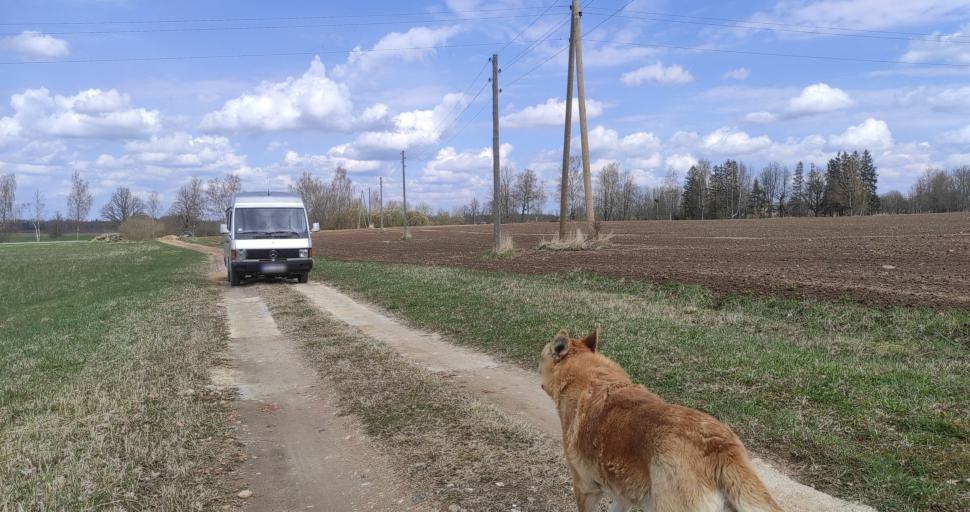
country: LV
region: Talsu Rajons
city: Sabile
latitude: 56.9479
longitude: 22.3517
